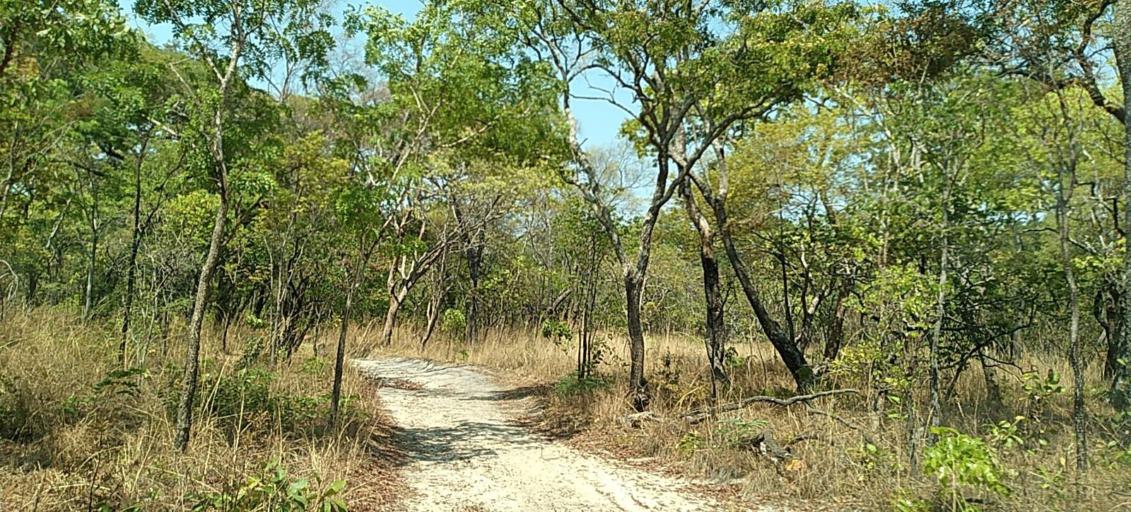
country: ZM
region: Copperbelt
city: Mpongwe
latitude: -13.7969
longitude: 28.0830
